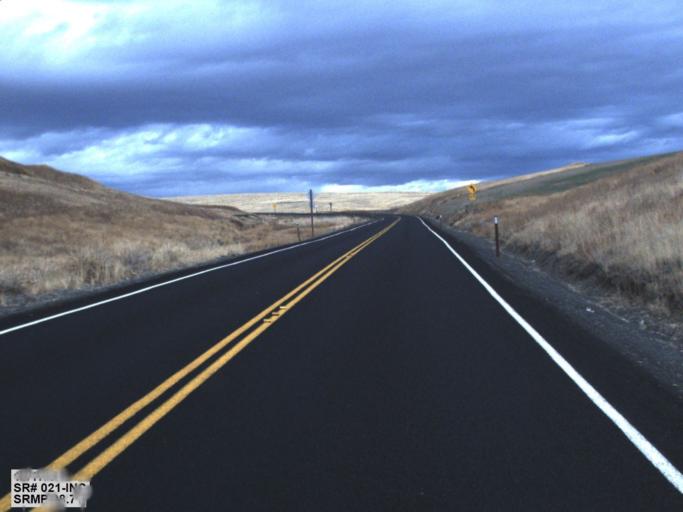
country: US
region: Washington
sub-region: Okanogan County
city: Coulee Dam
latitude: 47.8528
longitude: -118.7182
